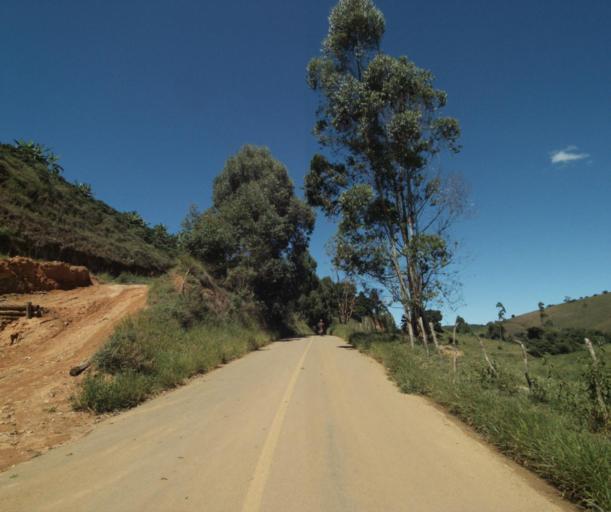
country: BR
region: Minas Gerais
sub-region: Espera Feliz
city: Espera Feliz
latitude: -20.5919
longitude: -41.8383
